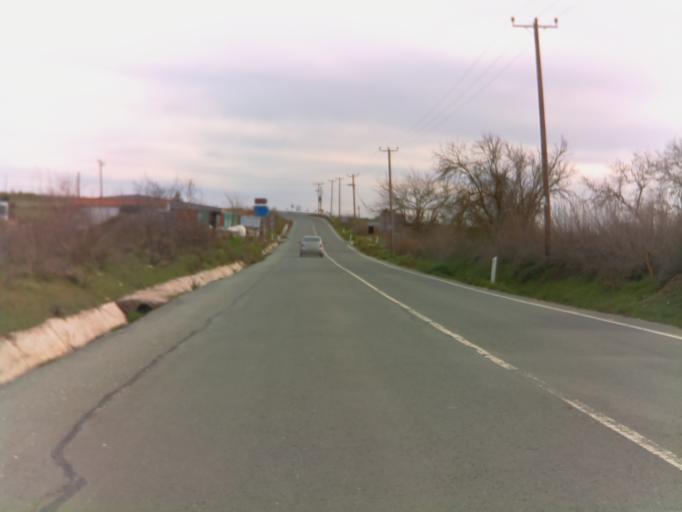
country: CY
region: Pafos
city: Pegeia
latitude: 34.9381
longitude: 32.4118
